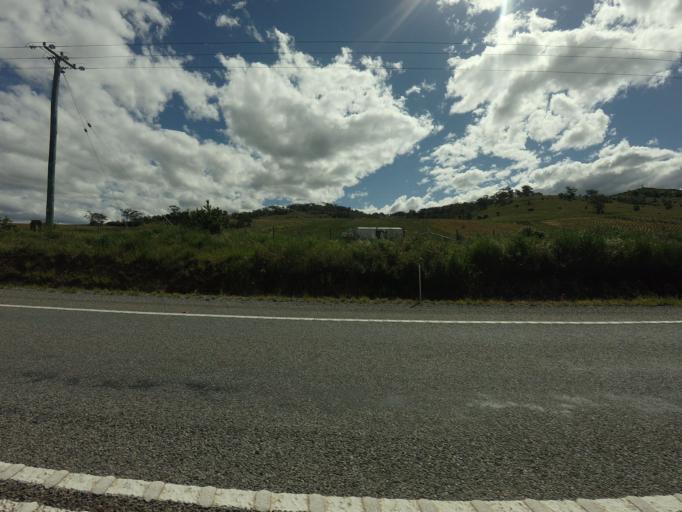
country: AU
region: Tasmania
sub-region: Northern Midlands
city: Evandale
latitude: -42.0589
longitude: 147.4828
